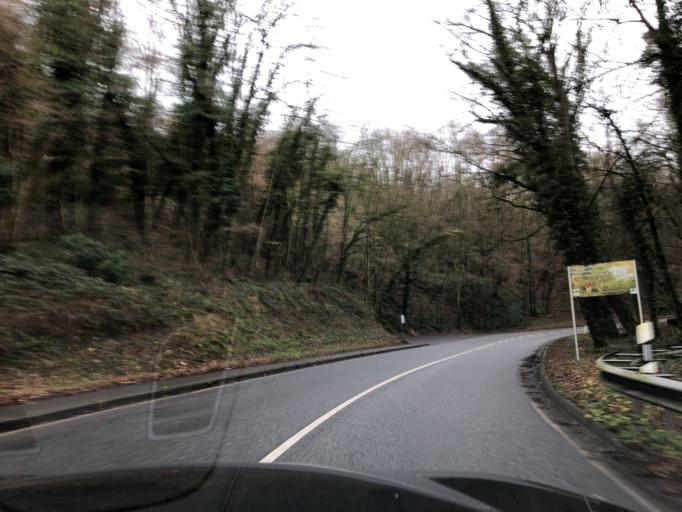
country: DE
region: Rheinland-Pfalz
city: Unkel
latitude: 50.5998
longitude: 7.2260
